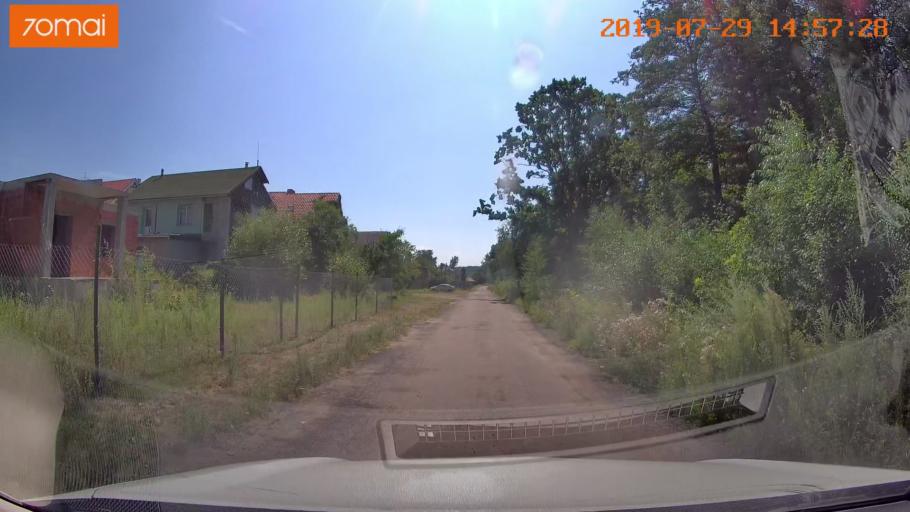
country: RU
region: Kaliningrad
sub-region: Gorod Kaliningrad
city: Baltiysk
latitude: 54.6801
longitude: 19.9165
